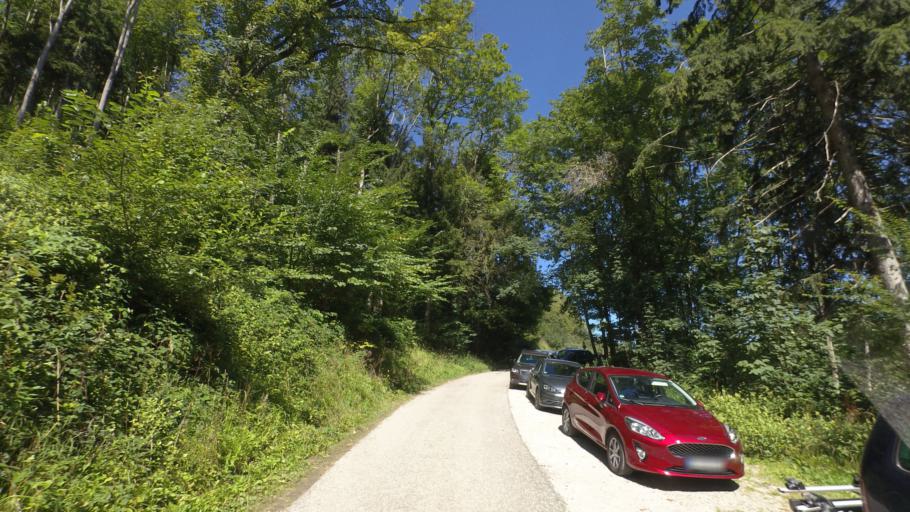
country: DE
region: Bavaria
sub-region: Upper Bavaria
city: Grassau
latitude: 47.7765
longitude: 12.4328
